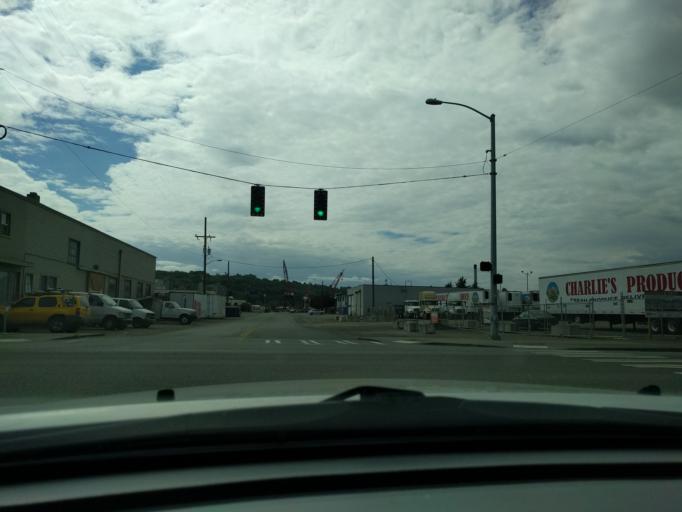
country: US
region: Washington
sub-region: King County
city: White Center
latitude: 47.5557
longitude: -122.3341
